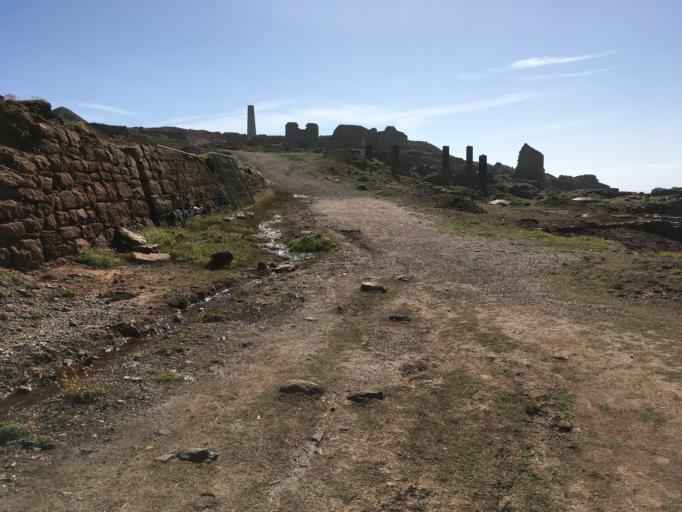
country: GB
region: England
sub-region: Cornwall
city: Saint Just
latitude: 50.1554
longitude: -5.6800
